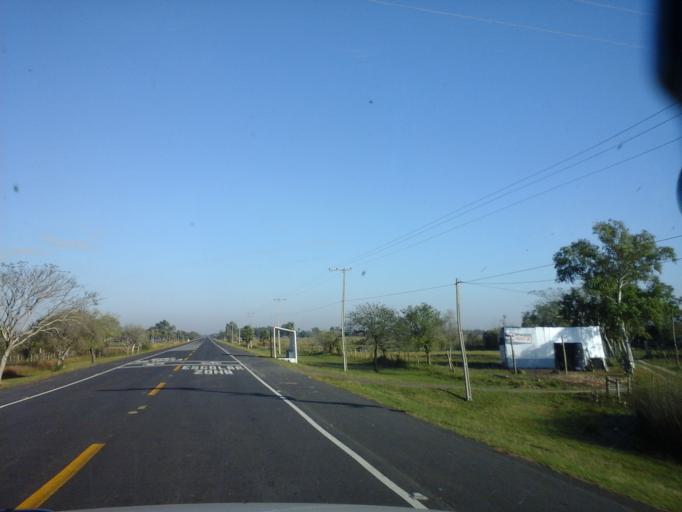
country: PY
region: Neembucu
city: Pilar
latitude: -26.8548
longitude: -58.0350
